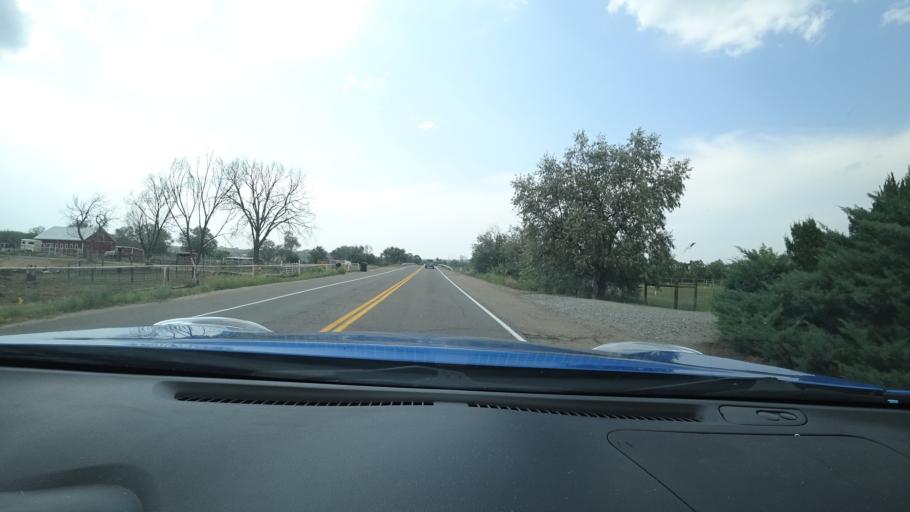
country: US
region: Colorado
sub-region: Adams County
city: Todd Creek
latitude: 39.9222
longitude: -104.8661
